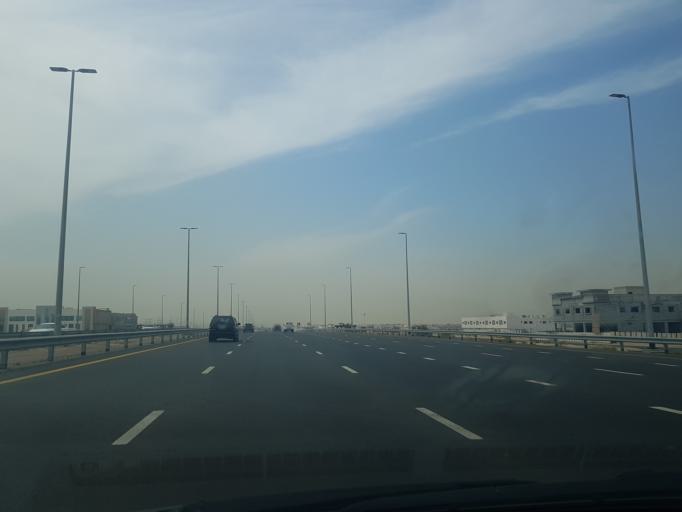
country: AE
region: Ash Shariqah
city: Sharjah
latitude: 25.2452
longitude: 55.5511
